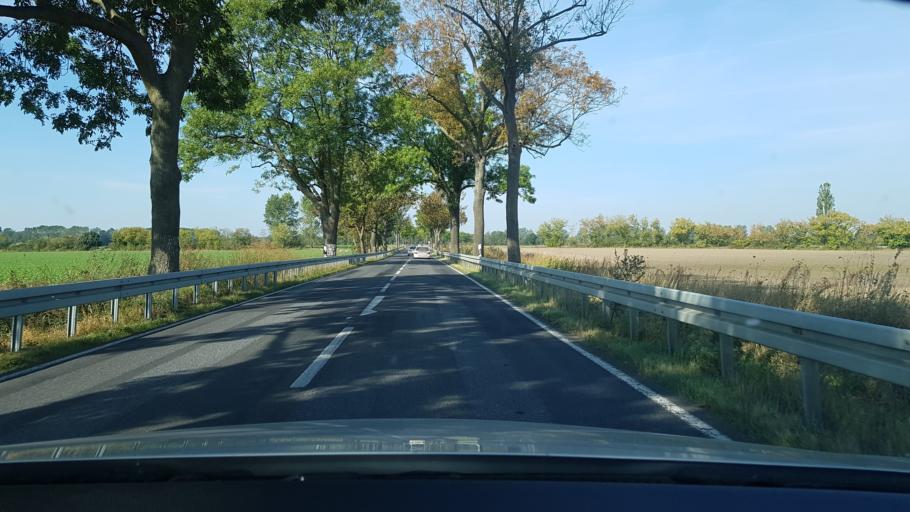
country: DE
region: Brandenburg
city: Beeskow
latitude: 52.1613
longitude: 14.2886
